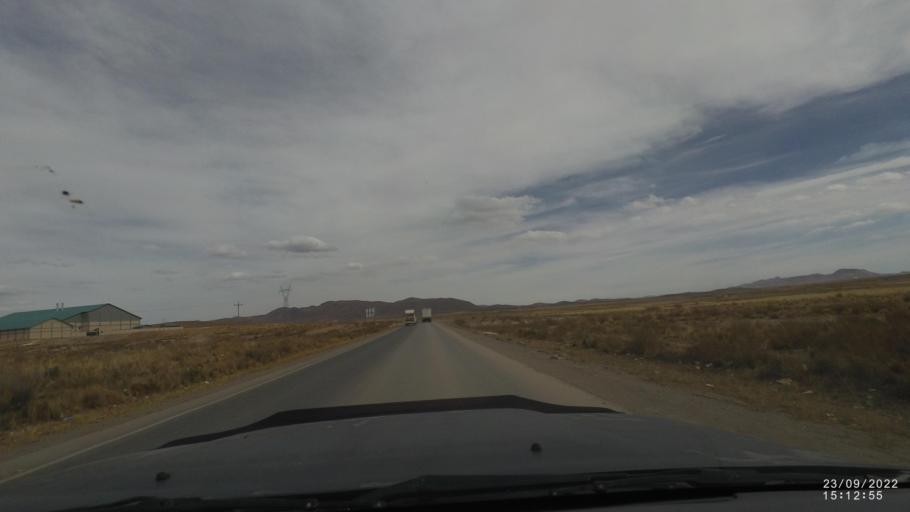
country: BO
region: Oruro
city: Oruro
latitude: -17.8293
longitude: -67.0285
